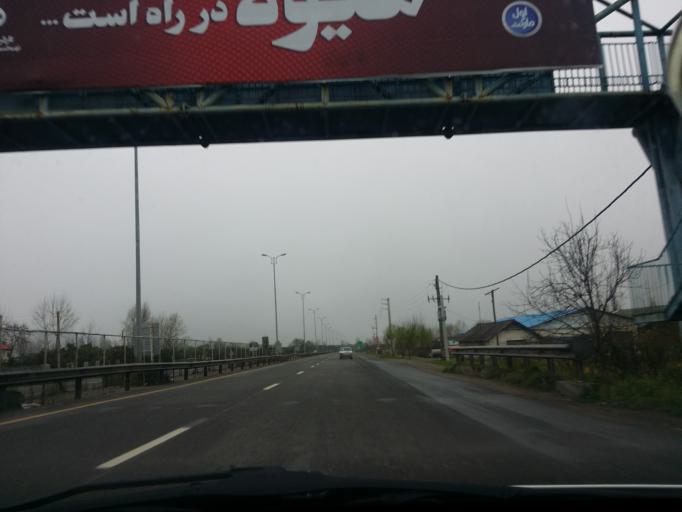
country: IR
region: Mazandaran
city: Tonekabon
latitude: 36.8149
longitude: 50.8532
